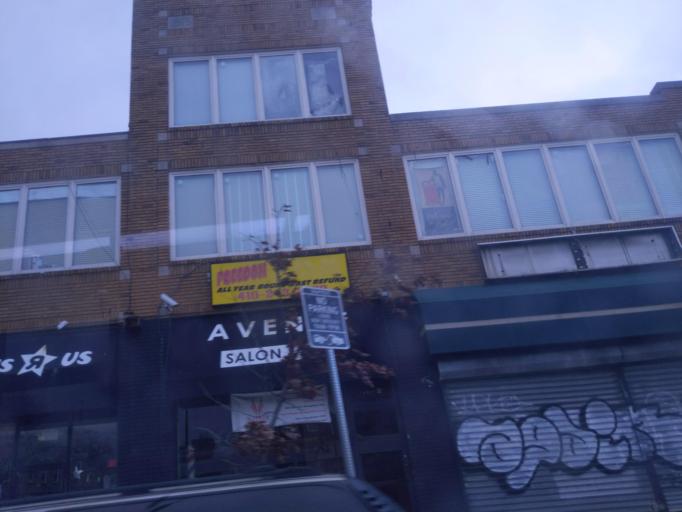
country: US
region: Maryland
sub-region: City of Baltimore
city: Baltimore
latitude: 39.3120
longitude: -76.6005
